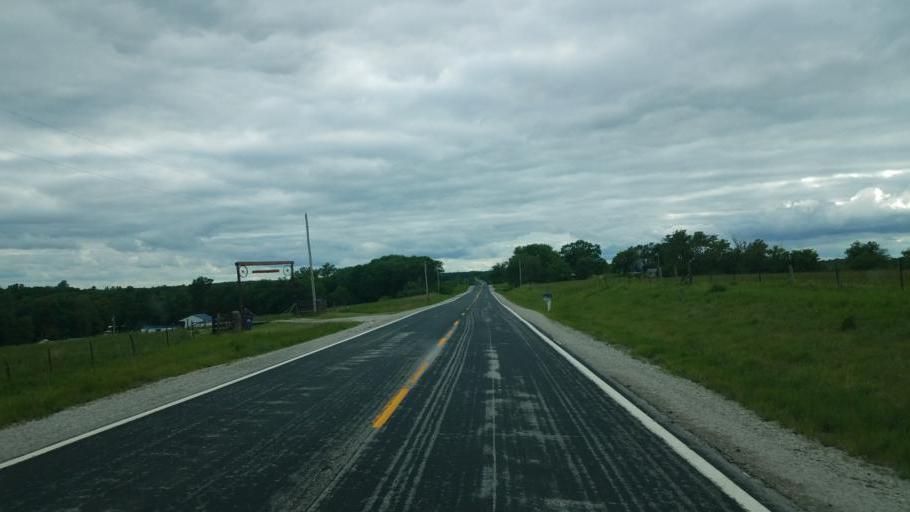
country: US
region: Missouri
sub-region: Mercer County
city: Princeton
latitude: 40.3692
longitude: -93.7251
